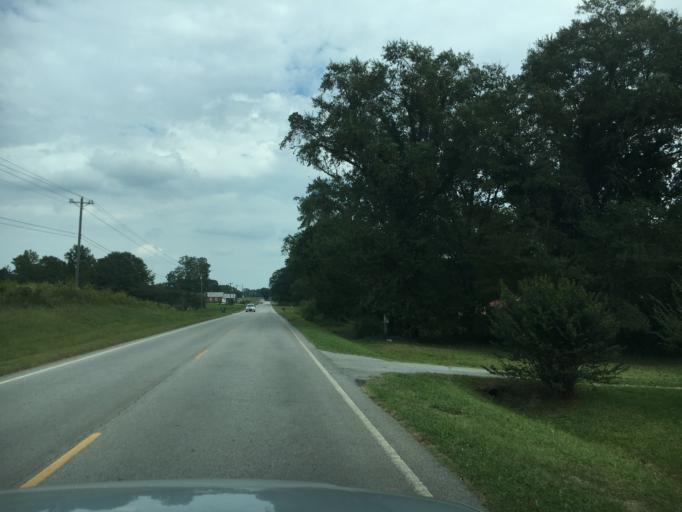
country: US
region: Georgia
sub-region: Franklin County
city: Gumlog
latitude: 34.4617
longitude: -83.0754
